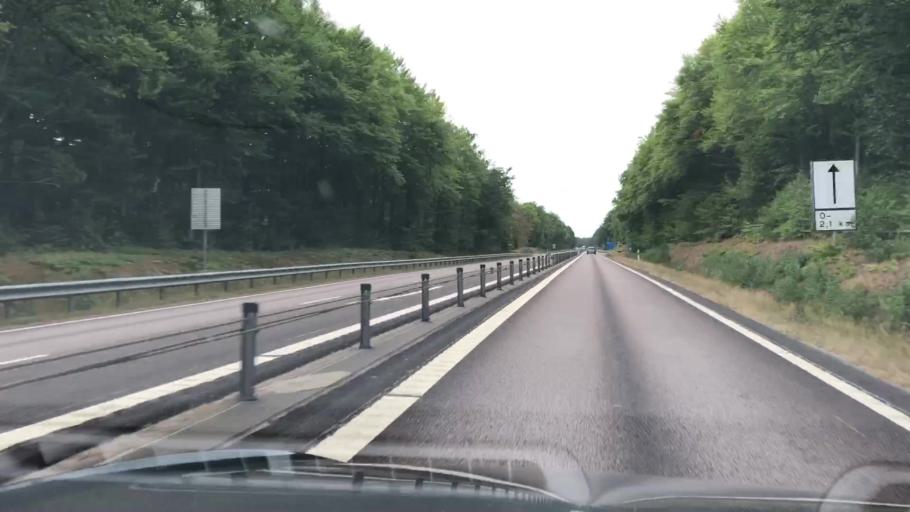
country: SE
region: Blekinge
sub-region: Karlskrona Kommun
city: Jaemjoe
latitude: 56.2376
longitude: 15.9243
